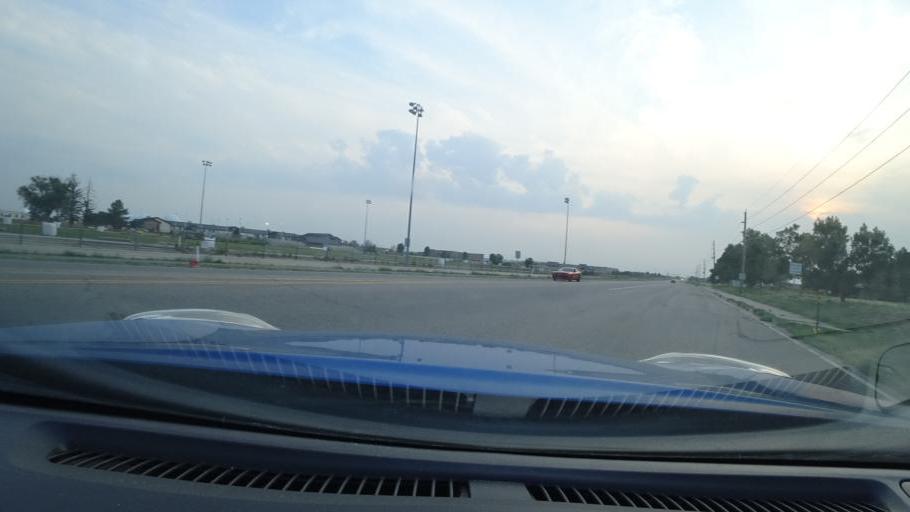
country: US
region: Colorado
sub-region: Adams County
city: Aurora
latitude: 39.7257
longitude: -104.7754
